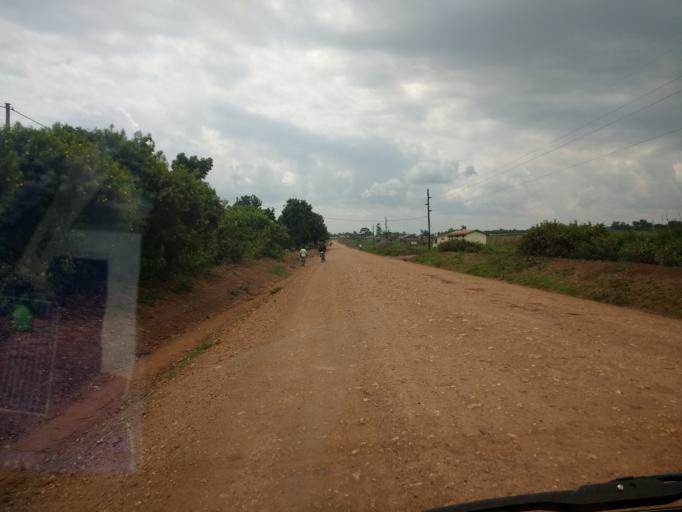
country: UG
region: Eastern Region
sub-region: Sironko District
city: Sironko
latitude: 1.3443
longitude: 34.3011
